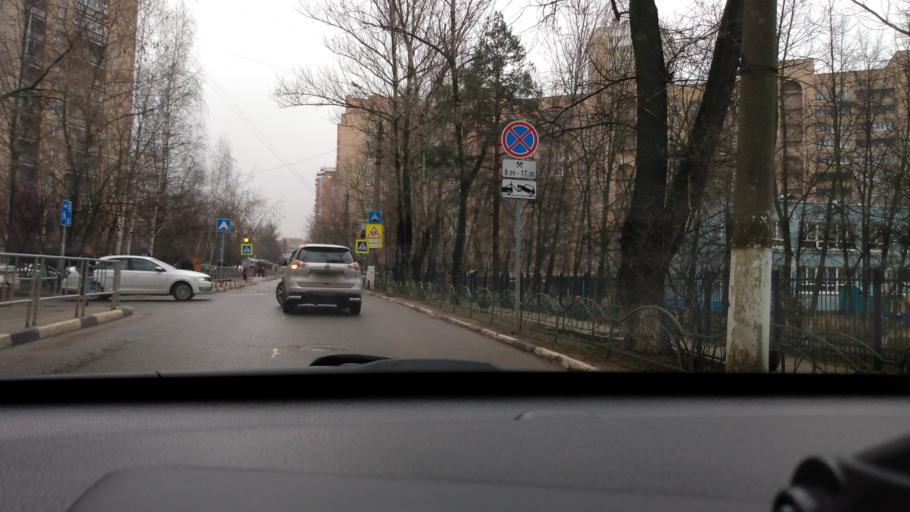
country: RU
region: Moskovskaya
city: Odintsovo
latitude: 55.6692
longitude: 37.2826
